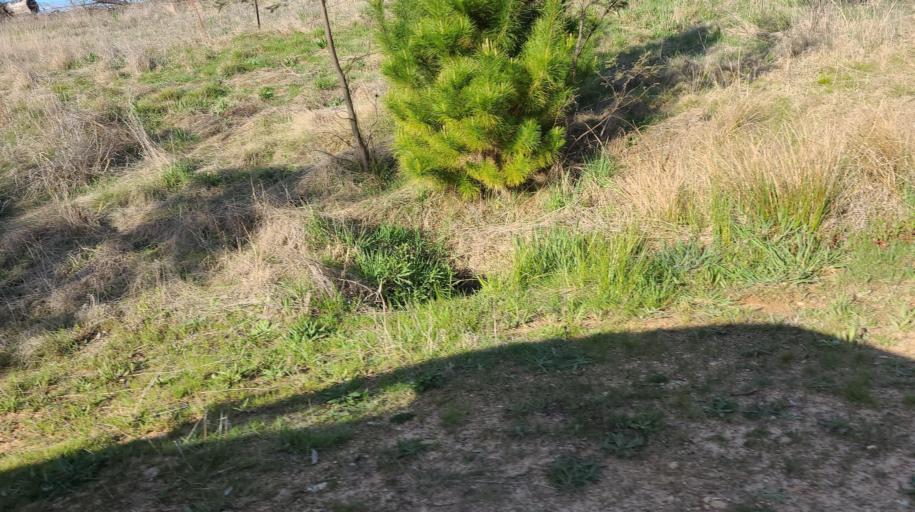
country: AU
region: New South Wales
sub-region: Blayney
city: Millthorpe
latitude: -33.4063
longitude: 149.3127
